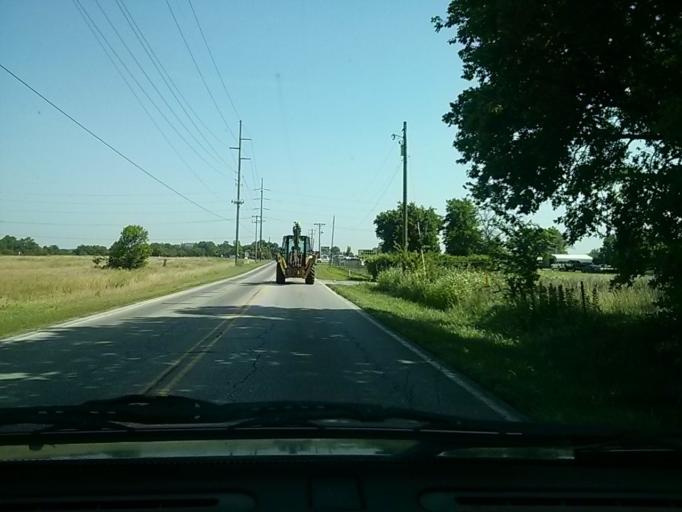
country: US
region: Oklahoma
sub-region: Rogers County
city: Catoosa
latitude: 36.1462
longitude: -95.7617
